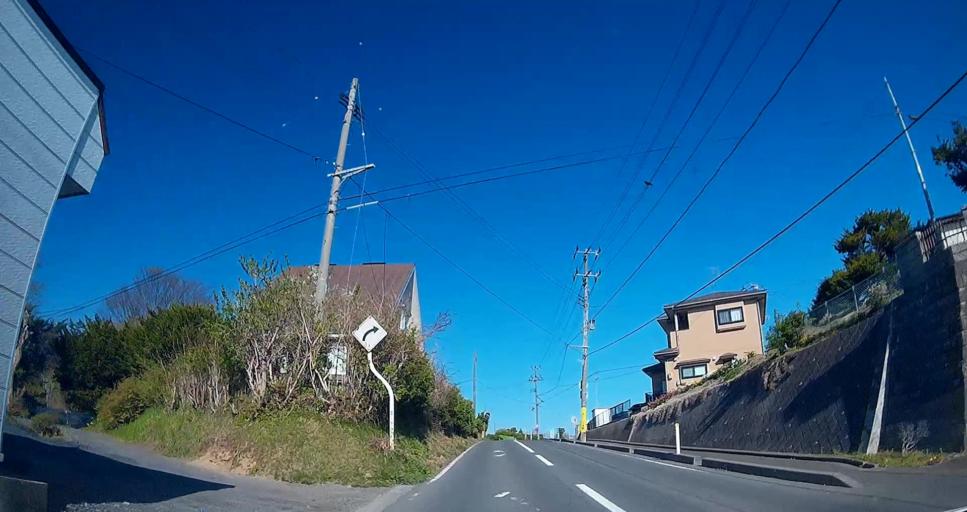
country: JP
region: Aomori
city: Hachinohe
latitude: 40.5156
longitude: 141.5903
